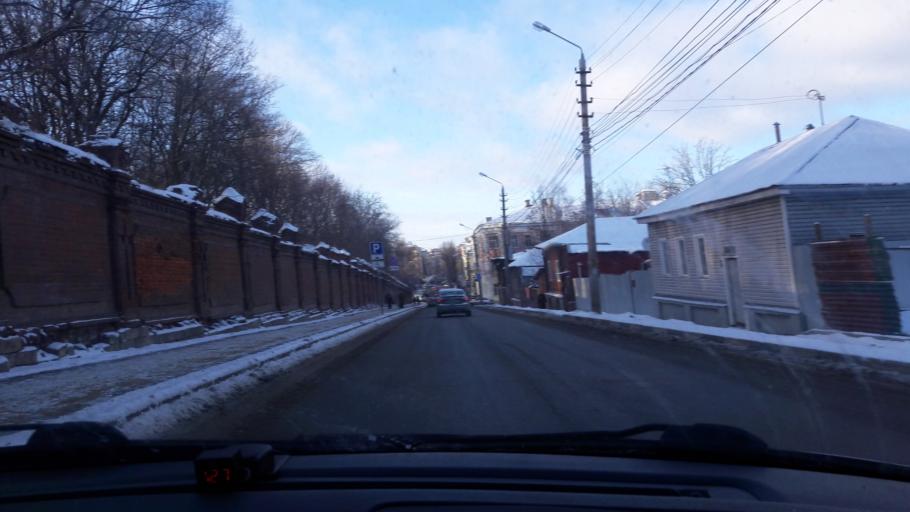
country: RU
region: Tula
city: Tula
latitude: 54.1821
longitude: 37.6112
